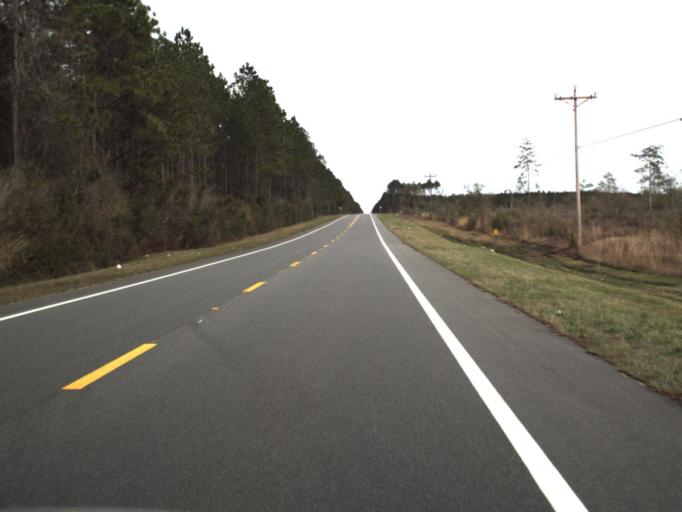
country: US
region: Florida
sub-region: Bay County
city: Callaway
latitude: 30.1480
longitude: -85.4578
